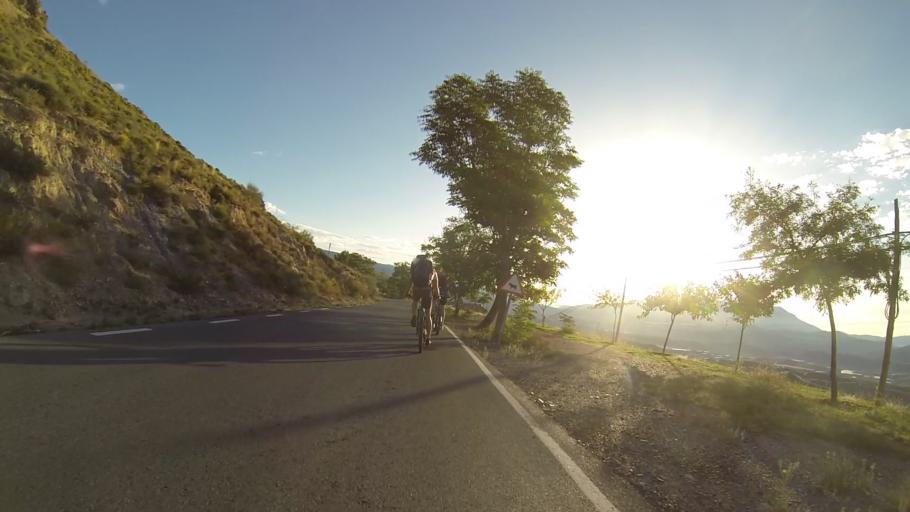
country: ES
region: Andalusia
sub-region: Provincia de Granada
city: Valor
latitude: 36.9783
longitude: -3.1253
